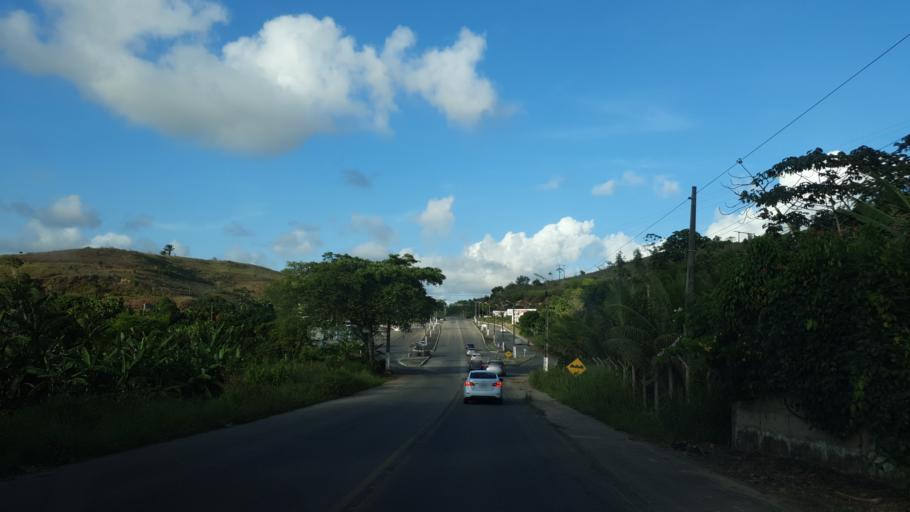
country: BR
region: Pernambuco
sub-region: Barreiros
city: Barreiros
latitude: -8.7922
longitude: -35.1864
